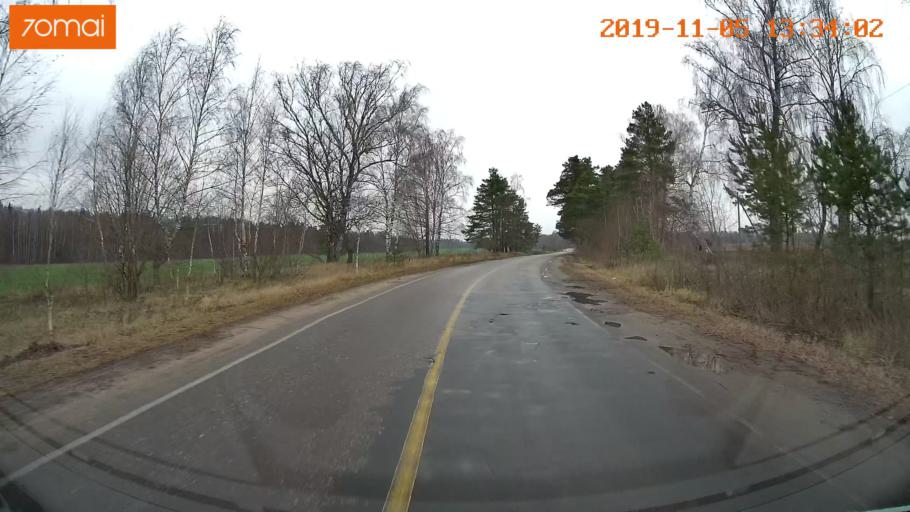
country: RU
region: Ivanovo
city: Shuya
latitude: 56.8973
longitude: 41.3903
